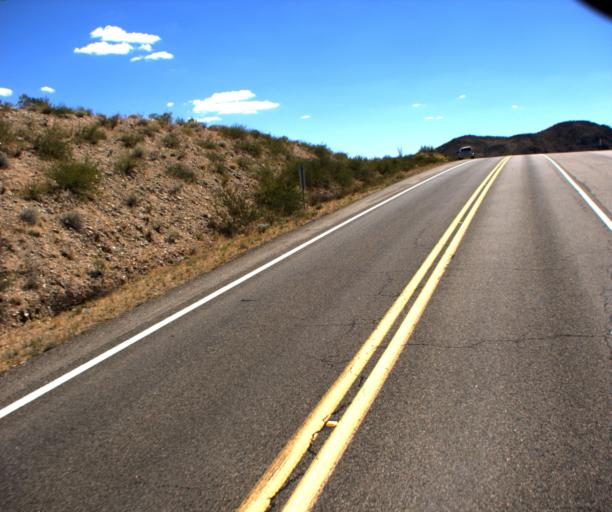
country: US
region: Arizona
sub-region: Yavapai County
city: Bagdad
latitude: 34.4340
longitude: -113.2418
